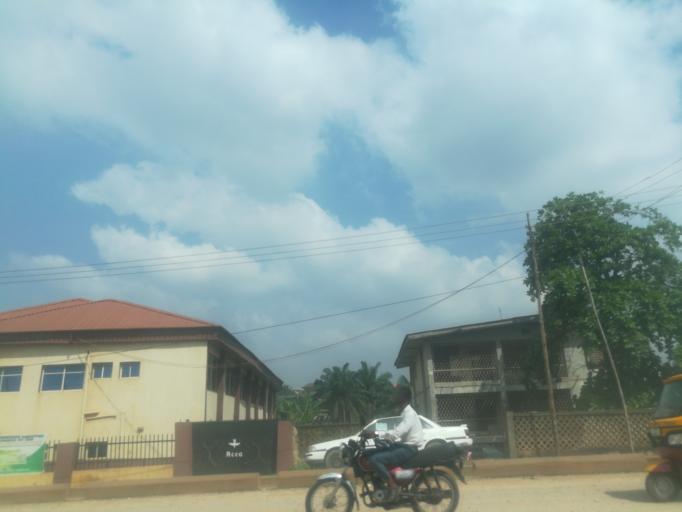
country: NG
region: Oyo
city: Ibadan
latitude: 7.3908
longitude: 3.9450
